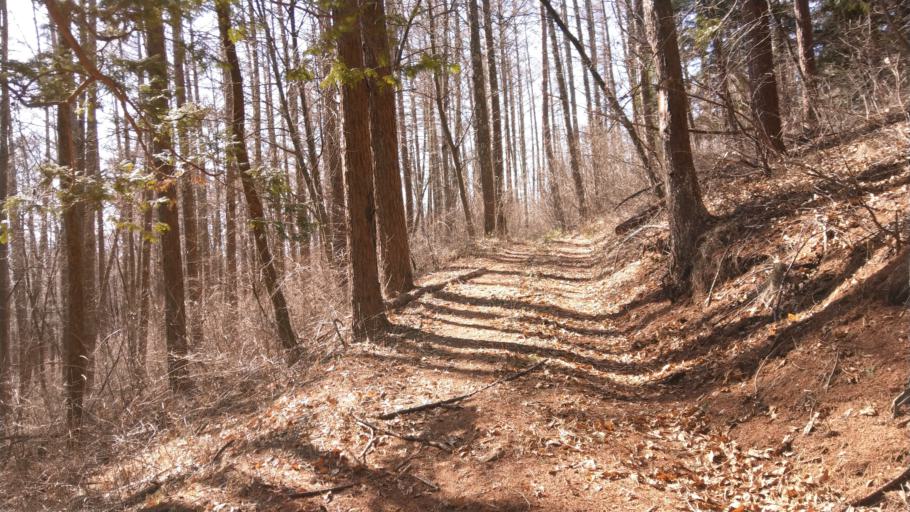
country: JP
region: Nagano
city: Komoro
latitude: 36.3697
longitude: 138.4330
